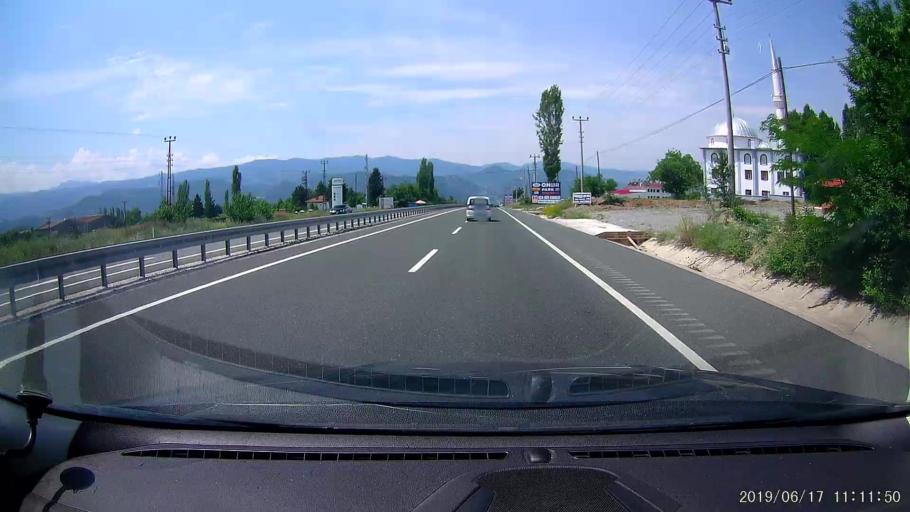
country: TR
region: Kastamonu
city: Tosya
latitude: 40.9813
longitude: 34.0043
